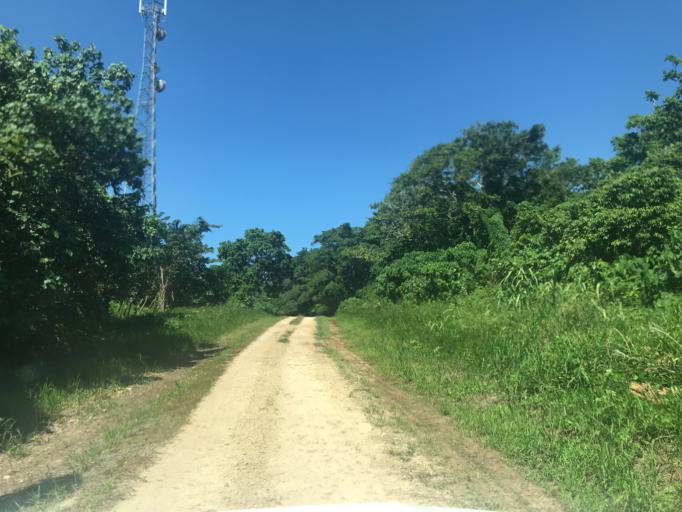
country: VU
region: Sanma
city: Luganville
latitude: -15.6400
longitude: 166.8091
